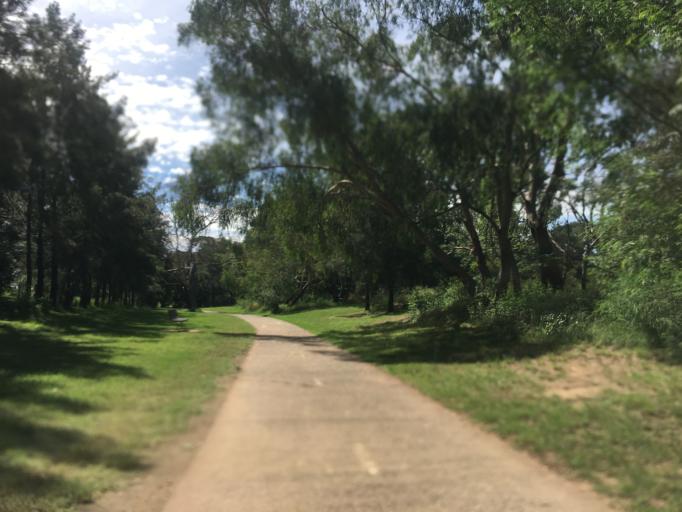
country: AU
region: New South Wales
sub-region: Camden
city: Elderslie
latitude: -34.0646
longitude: 150.6994
